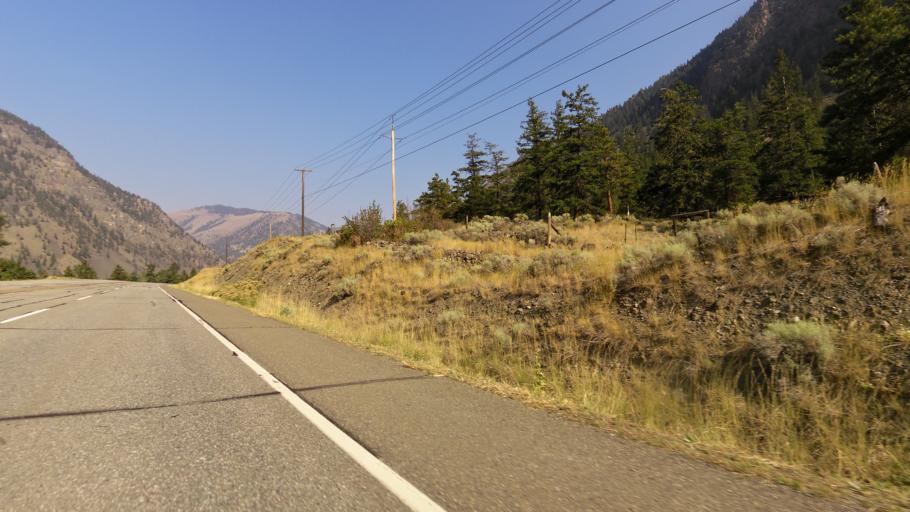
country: CA
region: British Columbia
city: Oliver
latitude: 49.2338
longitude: -119.9871
